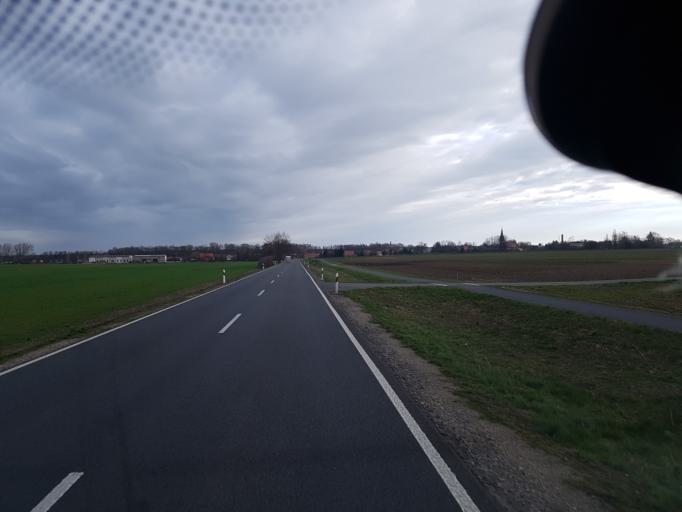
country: DE
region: Brandenburg
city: Tauche
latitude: 52.0786
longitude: 14.1600
